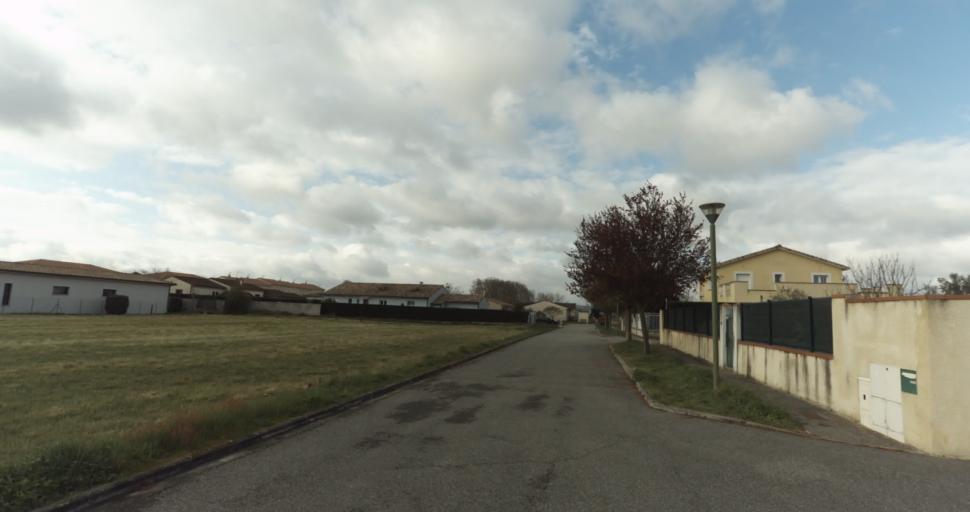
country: FR
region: Midi-Pyrenees
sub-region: Departement de la Haute-Garonne
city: Auterive
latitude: 43.3693
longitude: 1.4528
